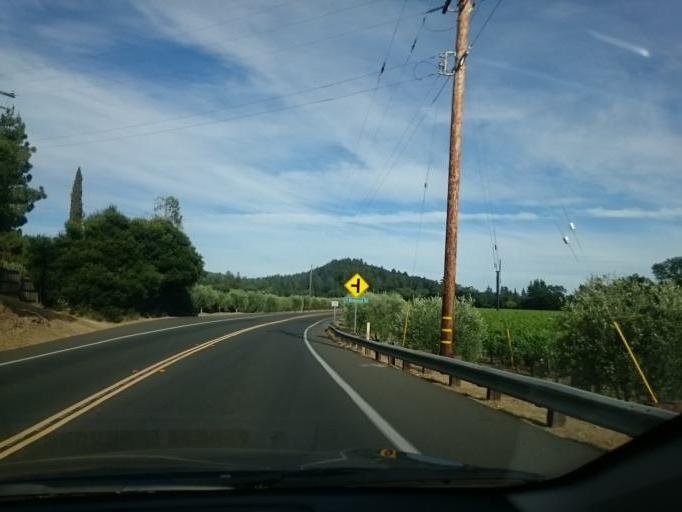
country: US
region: California
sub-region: Napa County
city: Saint Helena
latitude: 38.5173
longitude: -122.4639
